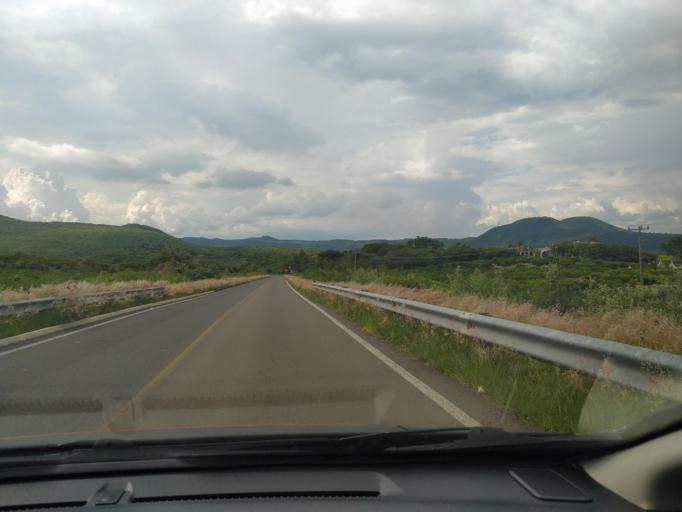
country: MX
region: Jalisco
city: Villa Corona
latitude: 20.3974
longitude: -103.6793
